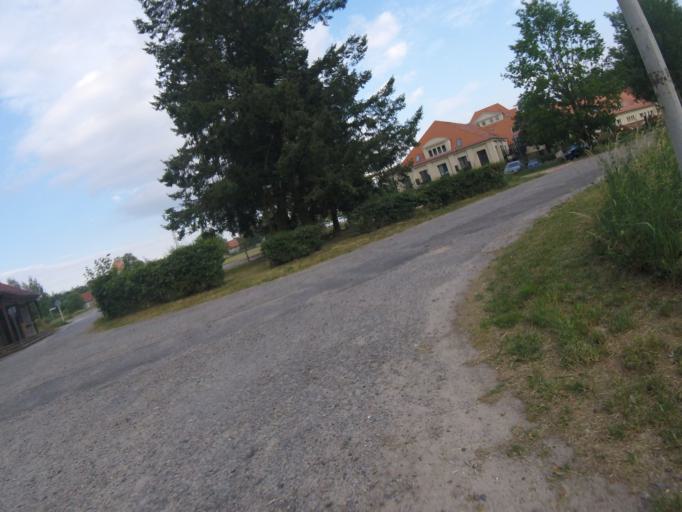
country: DE
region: Brandenburg
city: Konigs Wusterhausen
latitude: 52.3051
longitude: 13.6171
